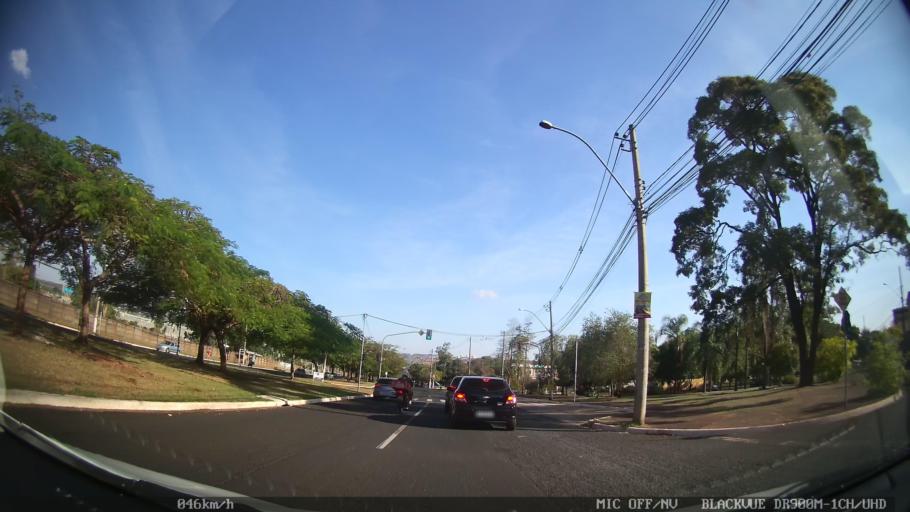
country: BR
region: Sao Paulo
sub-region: Ribeirao Preto
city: Ribeirao Preto
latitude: -21.2039
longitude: -47.7687
